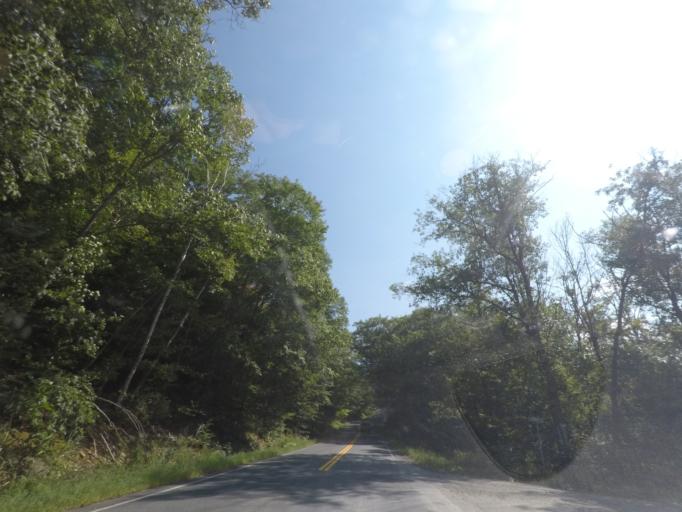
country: US
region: New York
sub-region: Rensselaer County
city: Poestenkill
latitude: 42.7189
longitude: -73.5093
